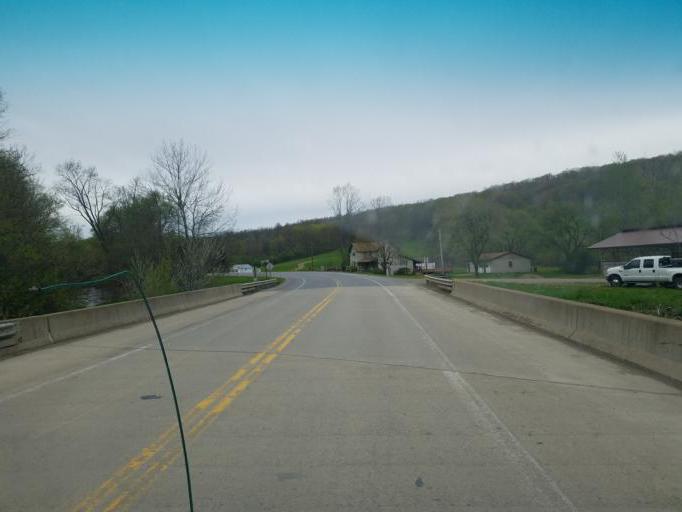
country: US
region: Pennsylvania
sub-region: Tioga County
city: Westfield
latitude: 41.9292
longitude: -77.6284
